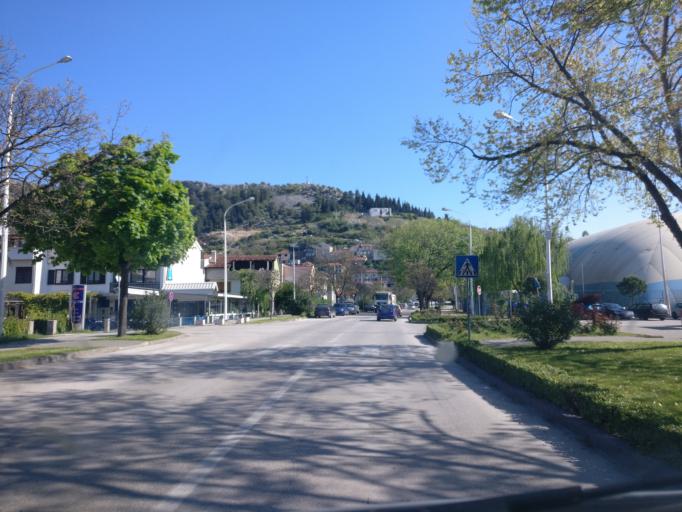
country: BA
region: Federation of Bosnia and Herzegovina
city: Capljina
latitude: 43.1131
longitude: 17.7004
